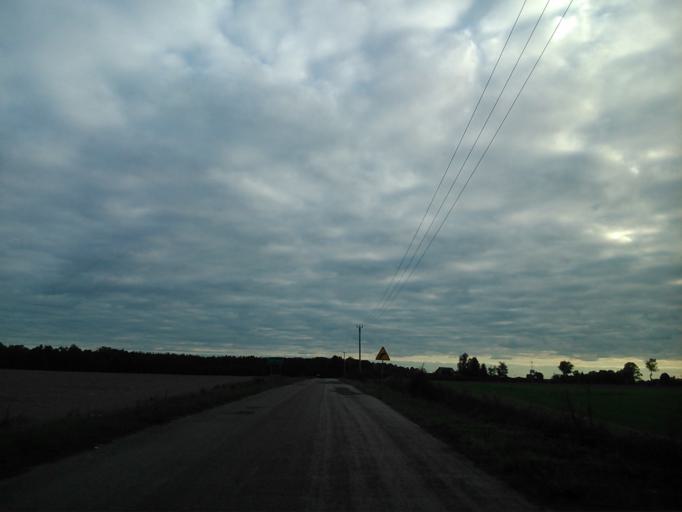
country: PL
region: Kujawsko-Pomorskie
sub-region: Powiat golubsko-dobrzynski
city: Kowalewo Pomorskie
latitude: 53.1061
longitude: 18.8919
